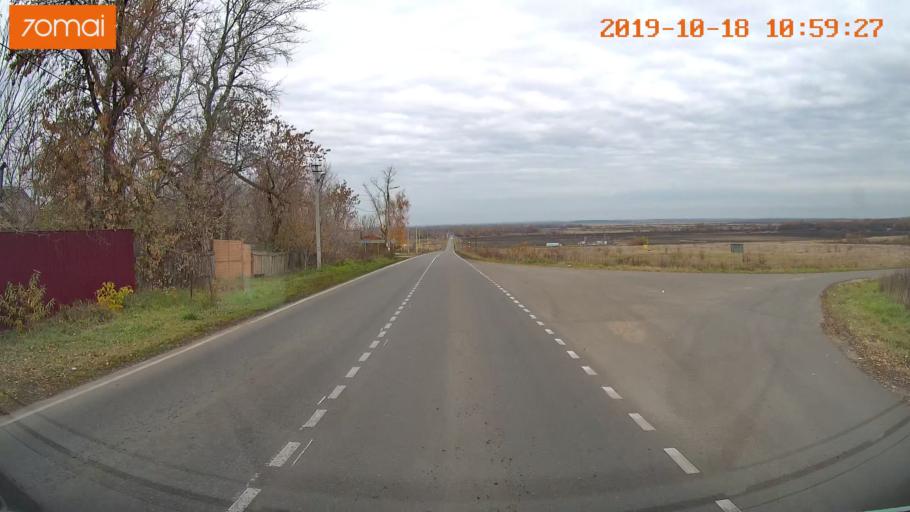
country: RU
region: Tula
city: Yepifan'
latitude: 53.8301
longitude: 38.5573
